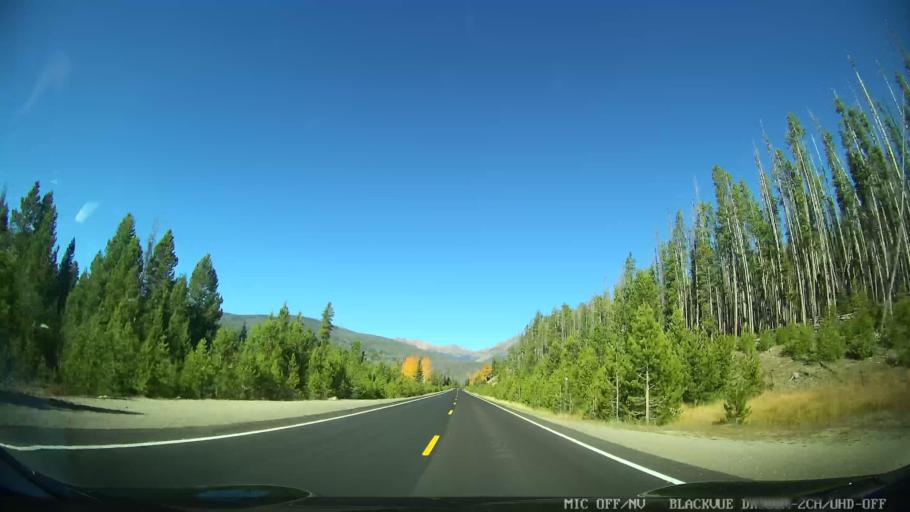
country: US
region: Colorado
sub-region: Grand County
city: Granby
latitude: 40.3189
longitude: -105.8469
